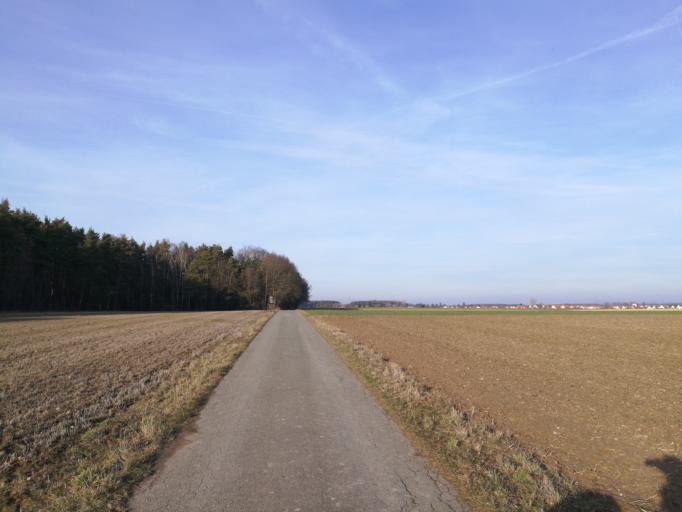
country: DE
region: Bavaria
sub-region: Regierungsbezirk Mittelfranken
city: Veitsbronn
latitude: 49.5224
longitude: 10.8906
